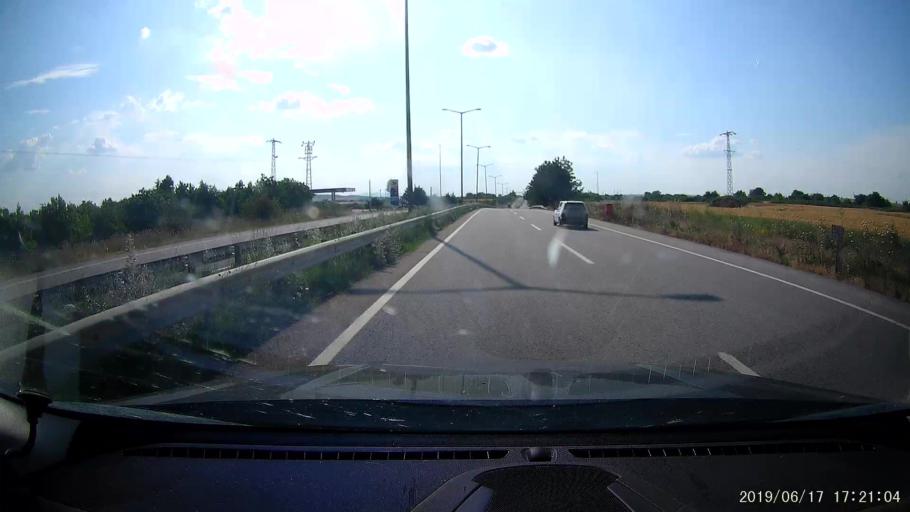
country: GR
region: East Macedonia and Thrace
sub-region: Nomos Evrou
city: Rizia
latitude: 41.7042
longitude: 26.4016
